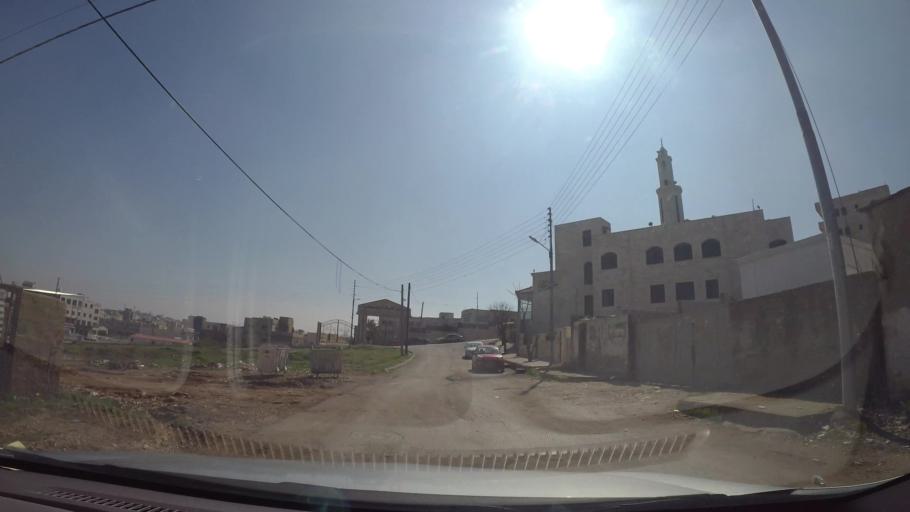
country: JO
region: Amman
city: Al Bunayyat ash Shamaliyah
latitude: 31.8975
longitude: 35.8978
